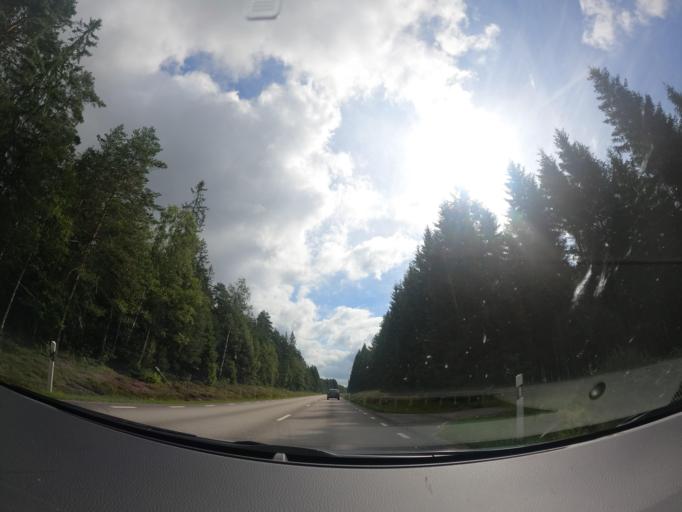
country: SE
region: Joenkoeping
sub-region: Gislaveds Kommun
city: Smalandsstenar
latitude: 57.1257
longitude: 13.3358
